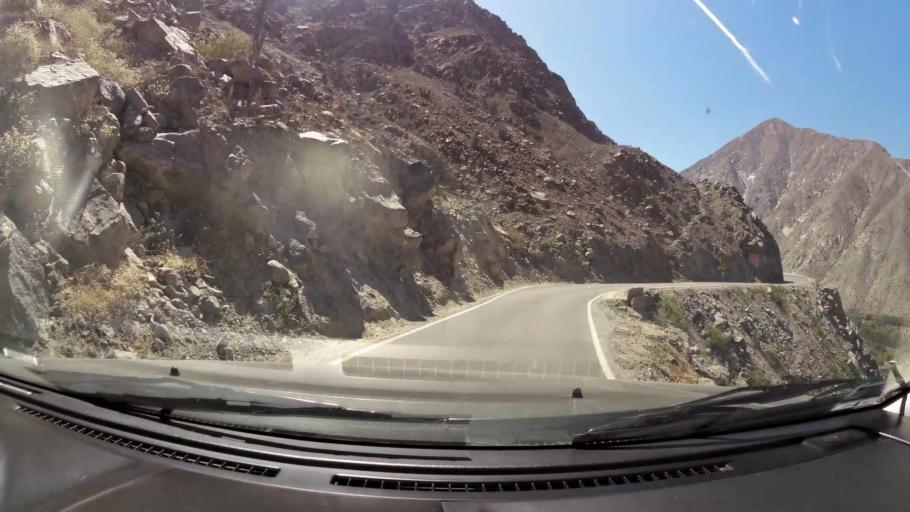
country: PE
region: Ica
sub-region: Provincia de Pisco
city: Huancano
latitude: -13.8333
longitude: -75.5460
